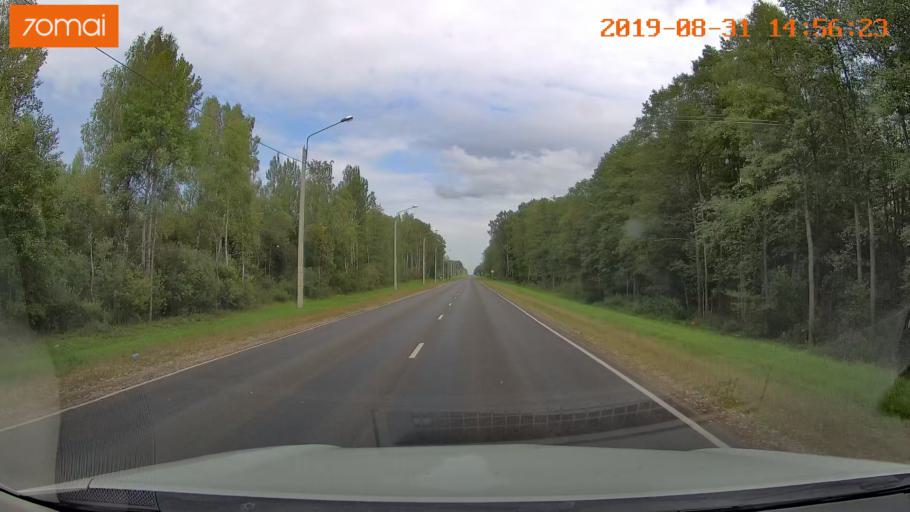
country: RU
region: Kaluga
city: Spas-Demensk
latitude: 54.3044
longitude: 33.9365
